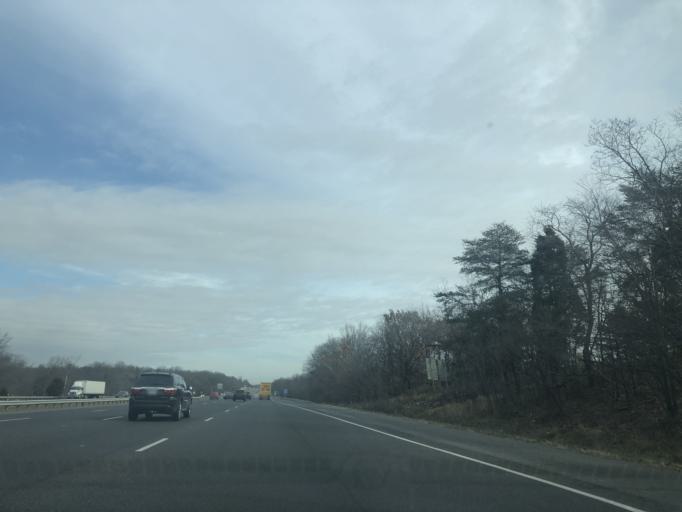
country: US
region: Maryland
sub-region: Howard County
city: West Elkridge
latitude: 39.2011
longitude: -76.7592
